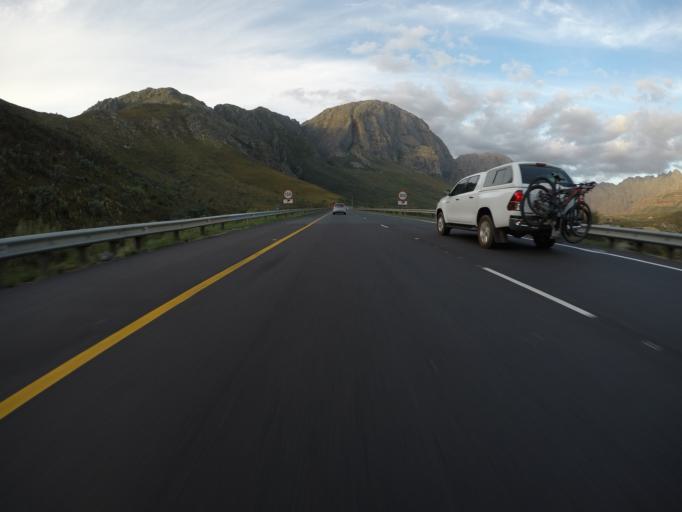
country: ZA
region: Western Cape
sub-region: Cape Winelands District Municipality
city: Paarl
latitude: -33.7303
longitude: 19.1180
